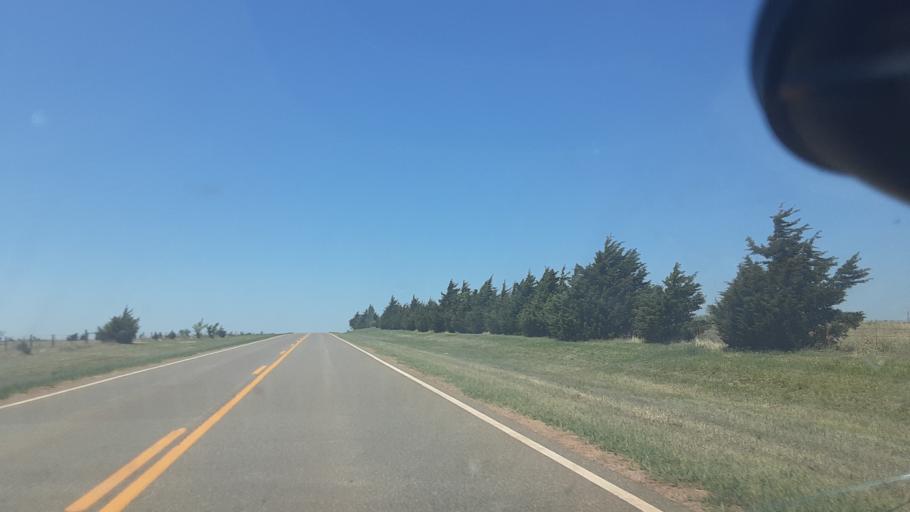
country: US
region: Oklahoma
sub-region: Noble County
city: Perry
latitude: 36.1157
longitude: -97.3589
